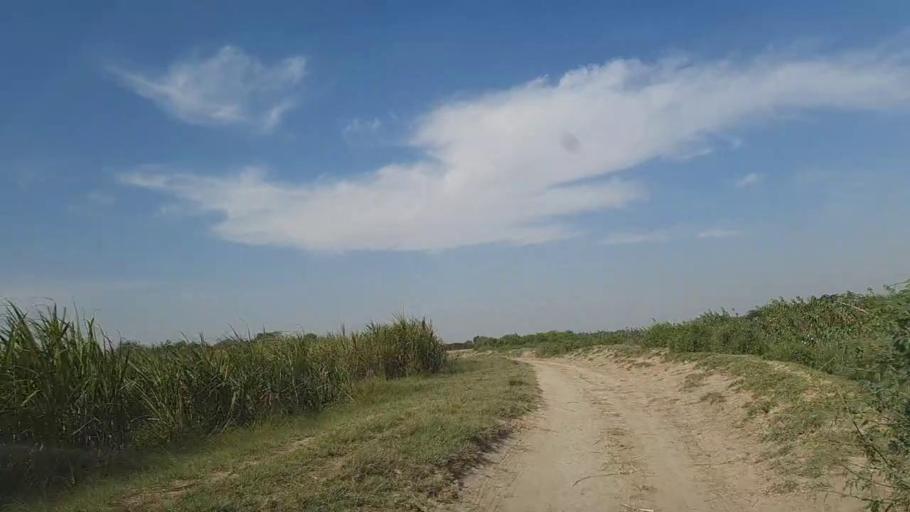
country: PK
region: Sindh
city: Mirpur Batoro
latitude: 24.8051
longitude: 68.2667
